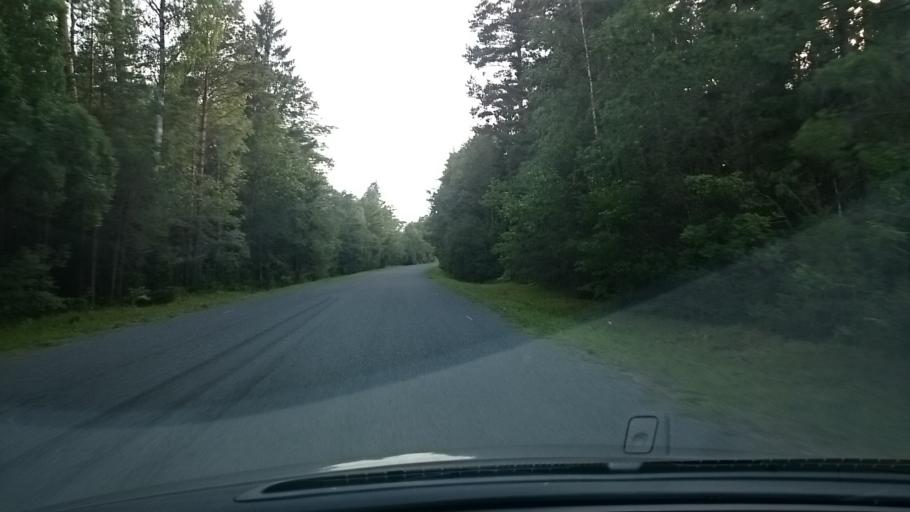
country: EE
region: Saare
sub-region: Kuressaare linn
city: Kuressaare
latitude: 58.4394
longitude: 22.2292
